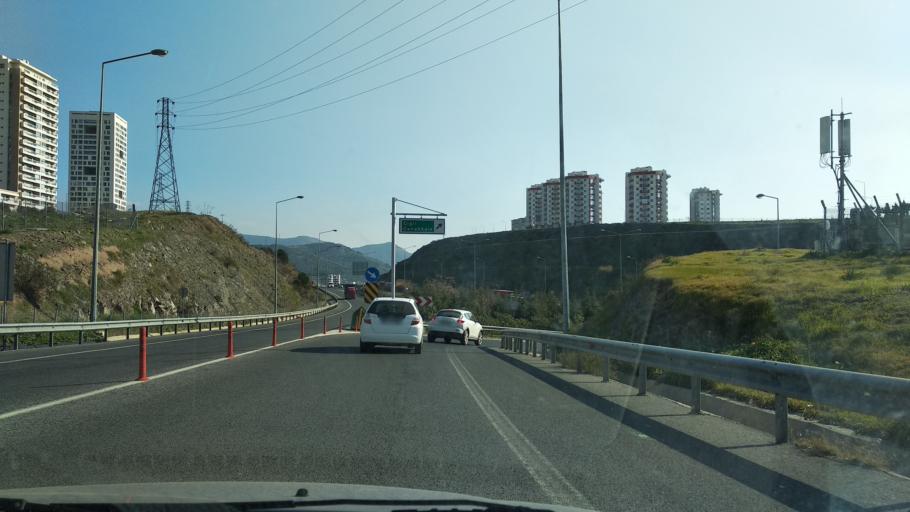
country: TR
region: Izmir
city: Karsiyaka
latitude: 38.4906
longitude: 27.0917
